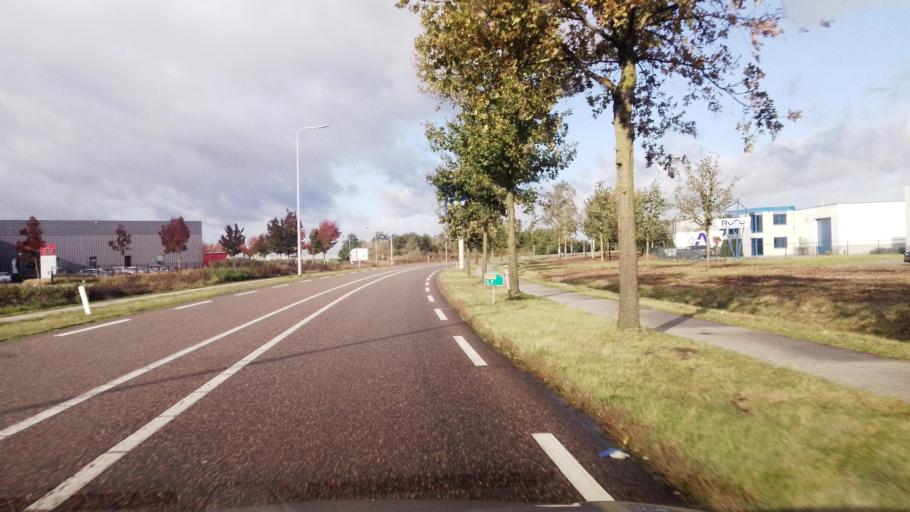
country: NL
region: Limburg
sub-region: Gemeente Peel en Maas
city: Maasbree
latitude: 51.3894
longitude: 6.0887
